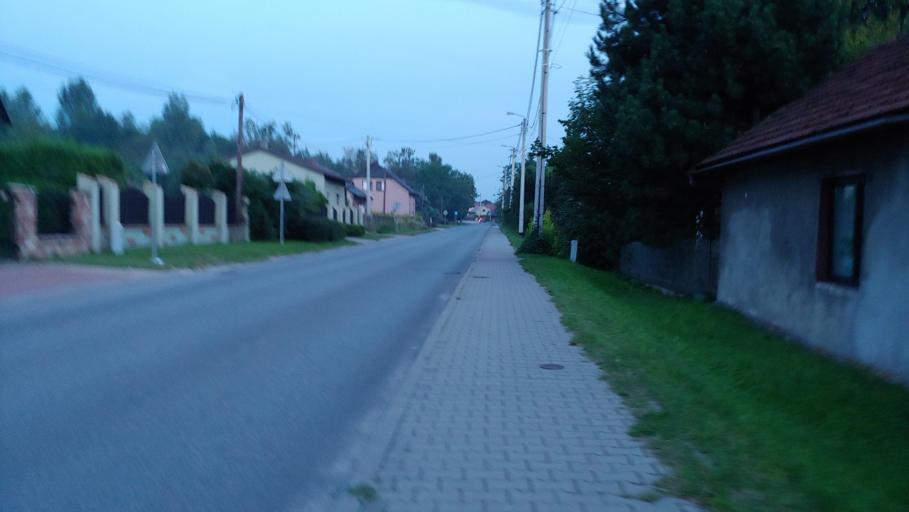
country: PL
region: Lesser Poland Voivodeship
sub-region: Powiat chrzanowski
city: Trzebinia
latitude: 50.1642
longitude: 19.4586
